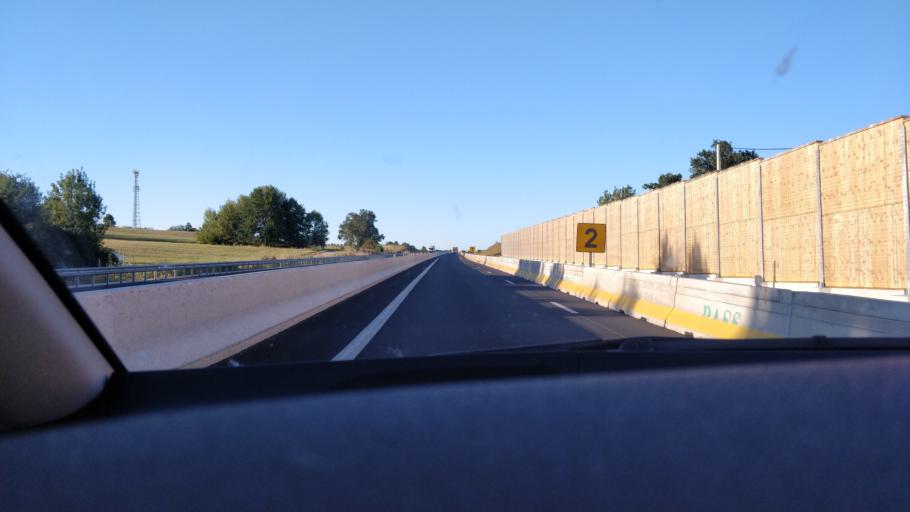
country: FR
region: Poitou-Charentes
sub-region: Departement de la Charente-Maritime
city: Chevanceaux
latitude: 45.3197
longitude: -0.2294
